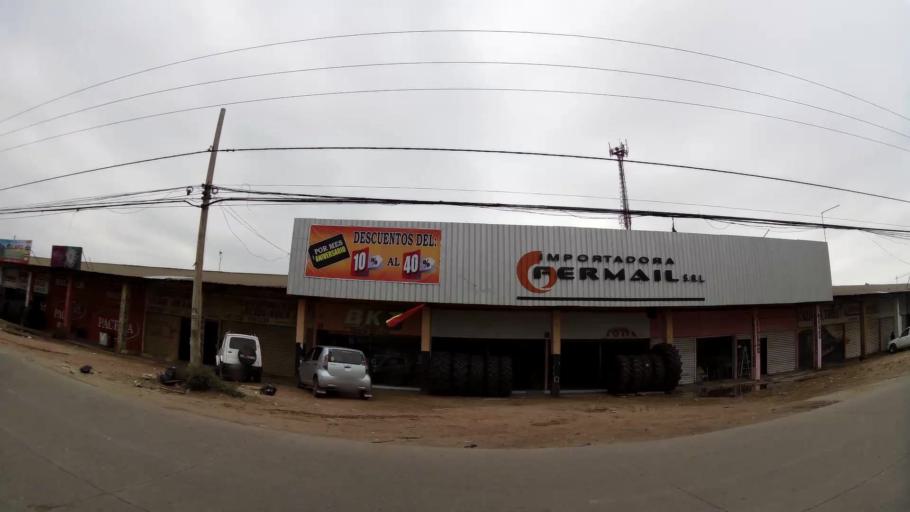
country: BO
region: Santa Cruz
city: Santa Cruz de la Sierra
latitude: -17.7497
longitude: -63.1839
